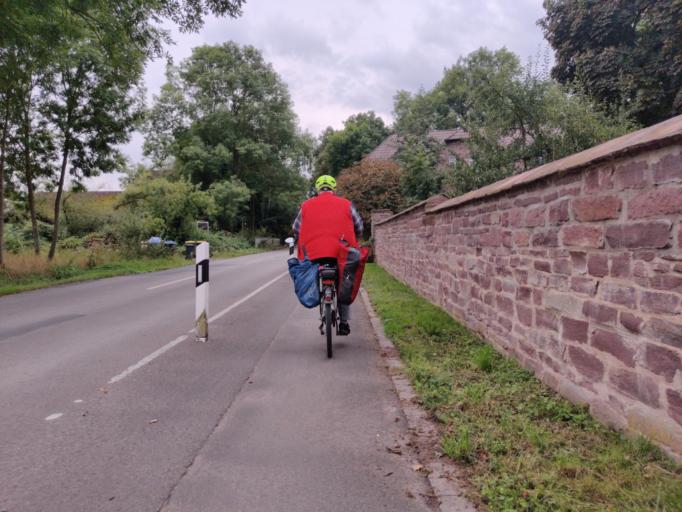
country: DE
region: Lower Saxony
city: Bevern
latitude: 51.8801
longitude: 9.4715
